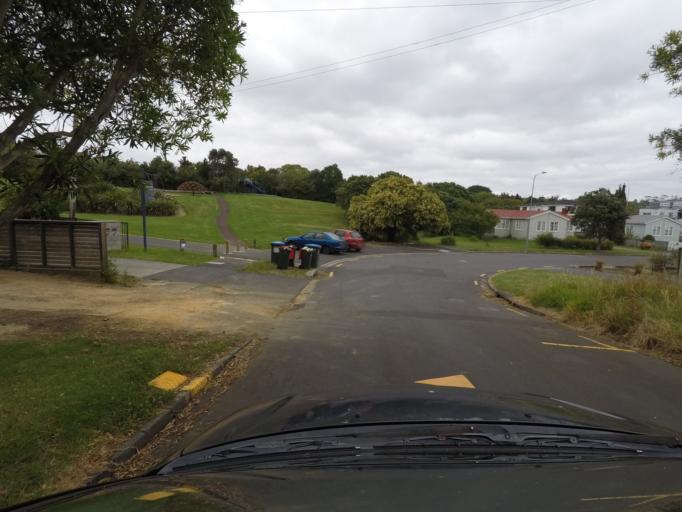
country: NZ
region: Auckland
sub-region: Auckland
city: Auckland
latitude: -36.8672
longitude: 174.7363
